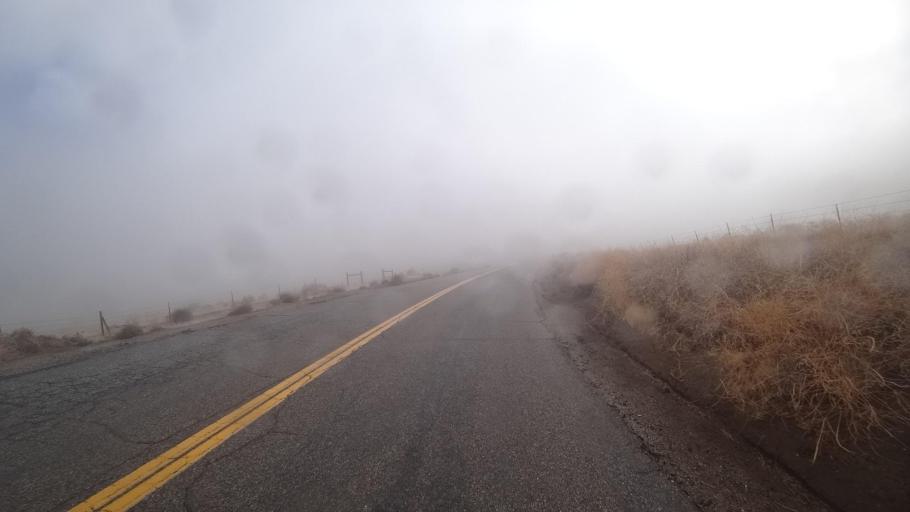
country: US
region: California
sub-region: Kern County
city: Maricopa
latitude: 34.9345
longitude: -119.4133
